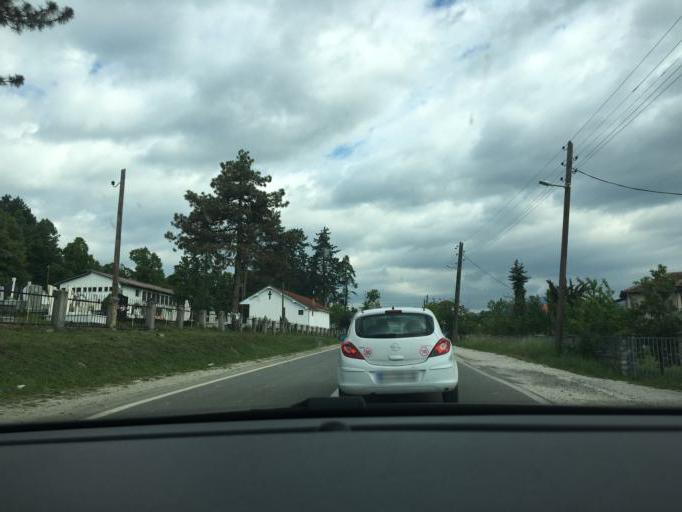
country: MK
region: Resen
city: Jankovec
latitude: 41.1064
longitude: 21.0122
